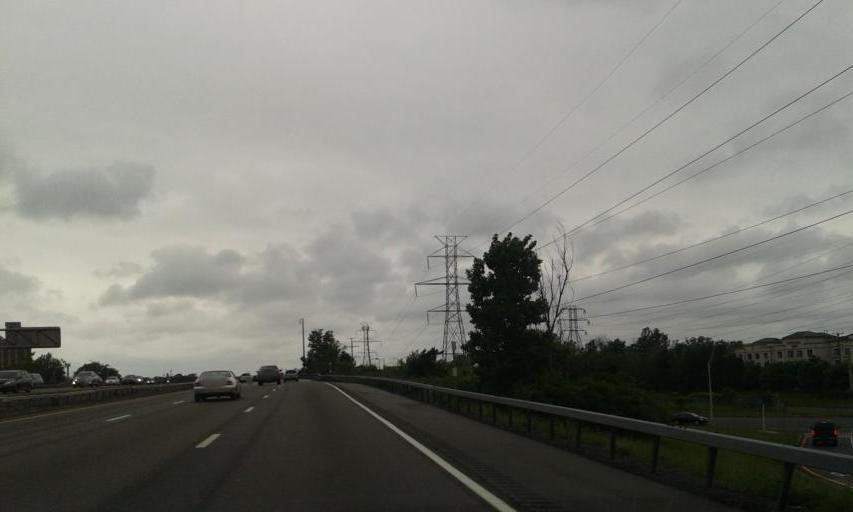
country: US
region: New York
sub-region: Erie County
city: Amherst
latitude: 42.9770
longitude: -78.7809
